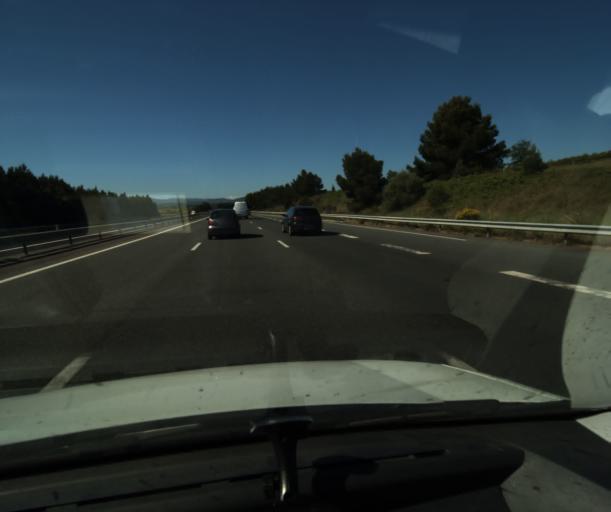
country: FR
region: Languedoc-Roussillon
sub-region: Departement de l'Aude
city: Peyriac-de-Mer
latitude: 43.1106
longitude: 2.9511
